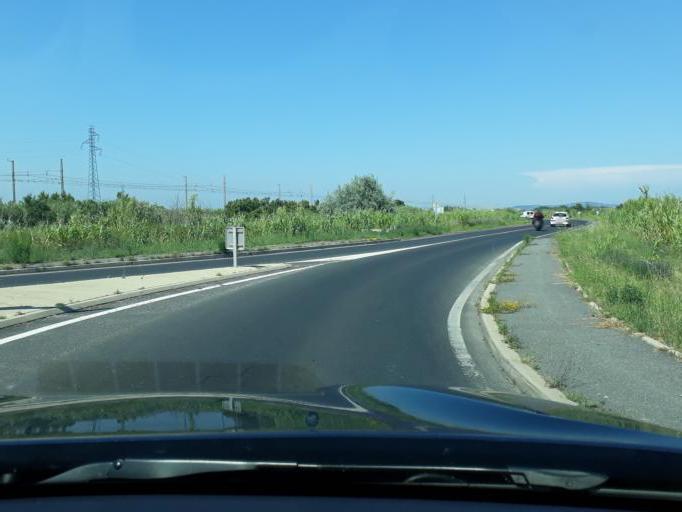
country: FR
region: Languedoc-Roussillon
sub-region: Departement de l'Herault
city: Marseillan
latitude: 43.3289
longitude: 3.5592
